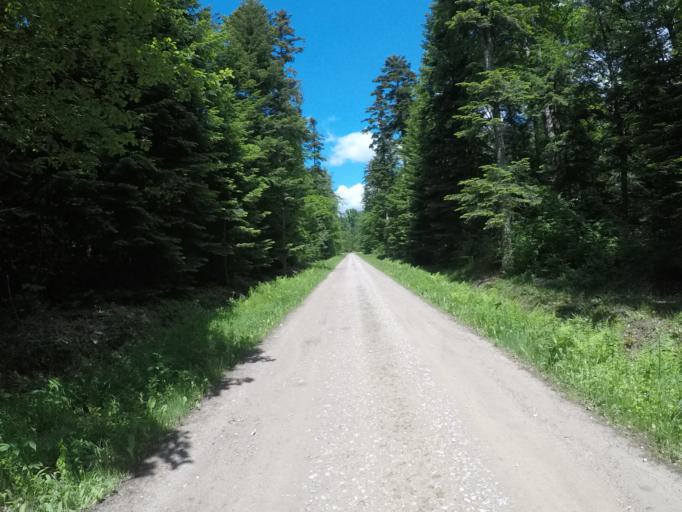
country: PL
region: Swietokrzyskie
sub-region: Powiat kielecki
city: Kostomloty Pierwsze
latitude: 50.9304
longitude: 20.6412
